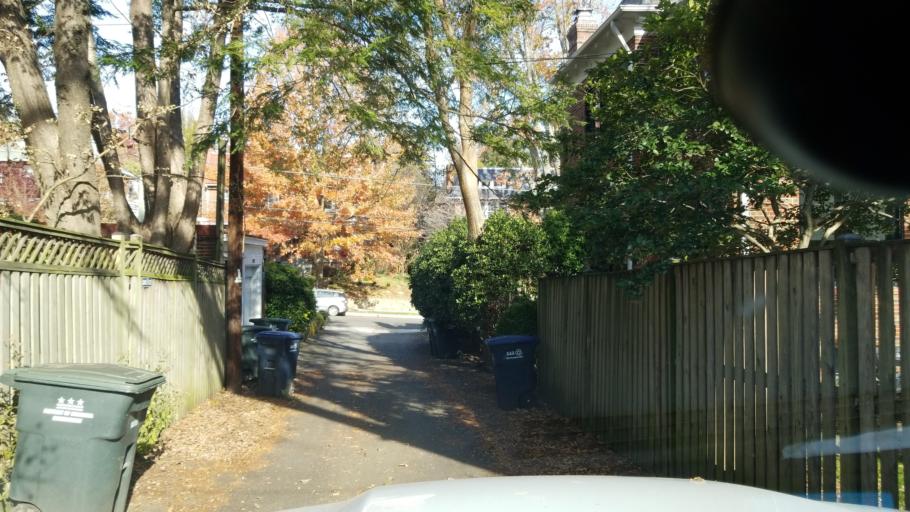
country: US
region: Maryland
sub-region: Montgomery County
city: Friendship Village
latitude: 38.9444
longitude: -77.0741
